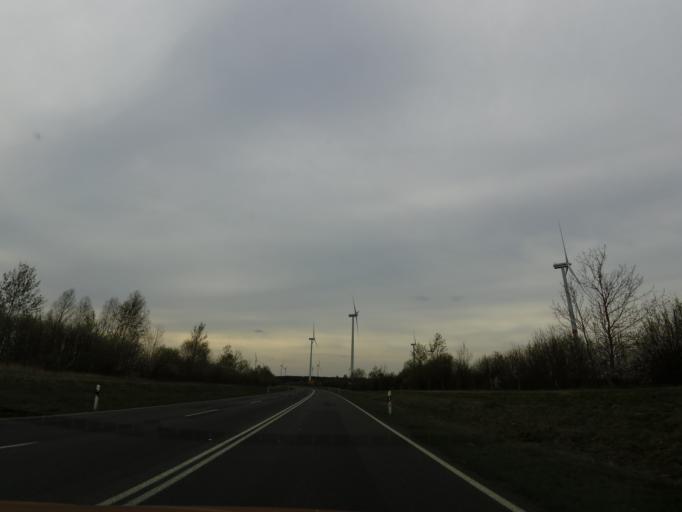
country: DE
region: Brandenburg
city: Beeskow
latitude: 52.2004
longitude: 14.2506
